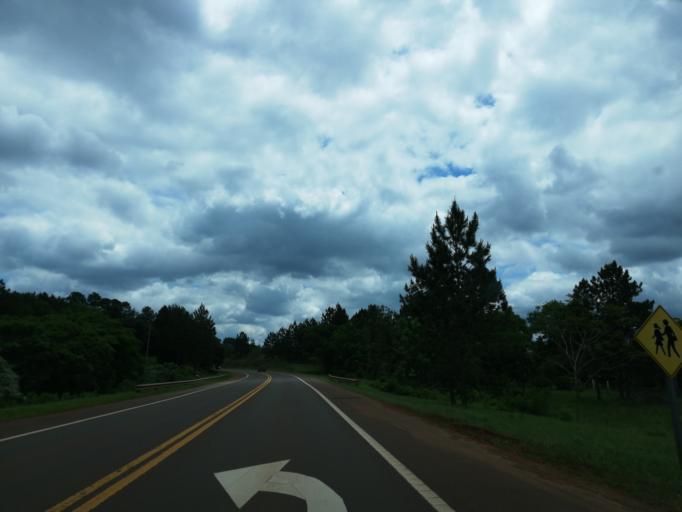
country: AR
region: Misiones
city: Arroyo del Medio
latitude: -27.6414
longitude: -55.3909
